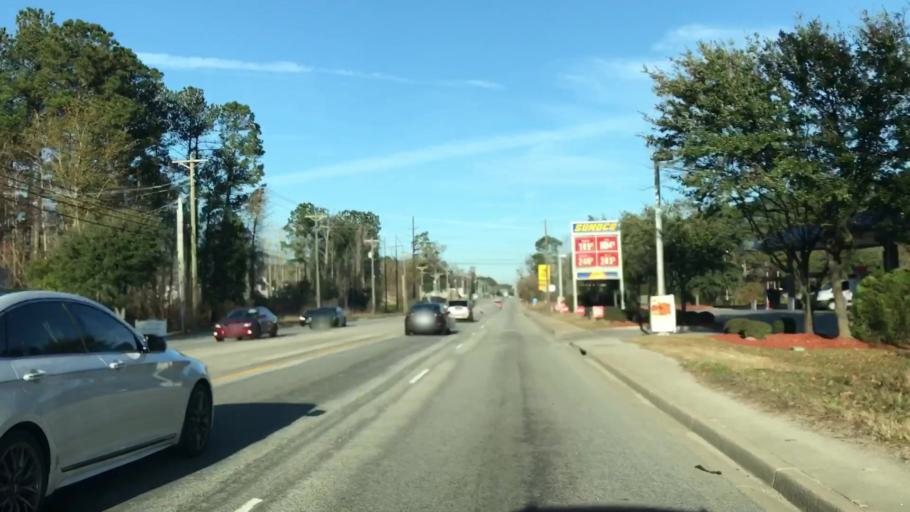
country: US
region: South Carolina
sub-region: Berkeley County
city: Ladson
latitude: 32.9843
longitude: -80.0920
